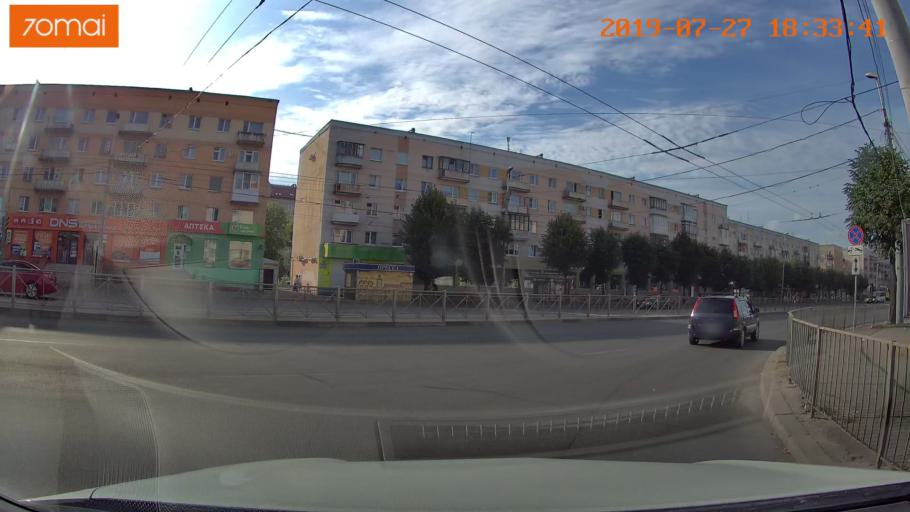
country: RU
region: Kaliningrad
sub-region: Gorod Kaliningrad
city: Kaliningrad
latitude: 54.6995
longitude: 20.5035
